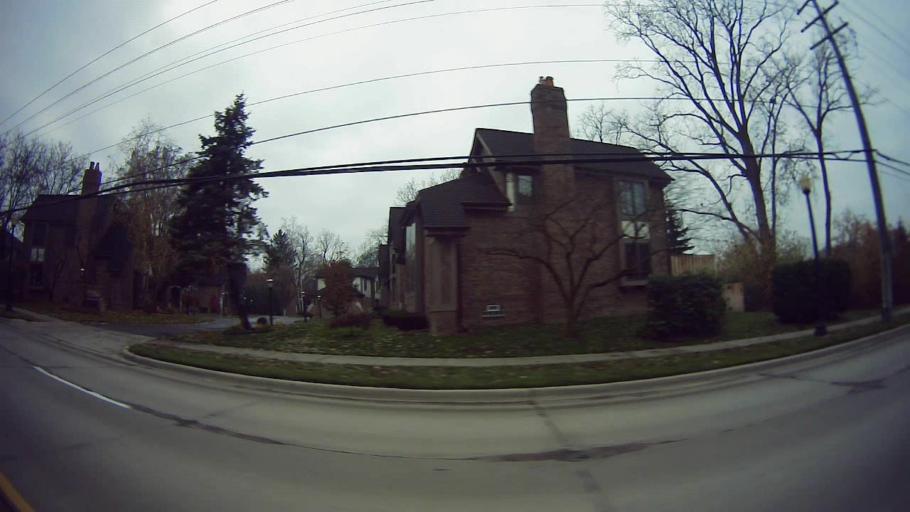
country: US
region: Michigan
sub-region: Wayne County
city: Dearborn Heights
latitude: 42.3078
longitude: -83.2523
